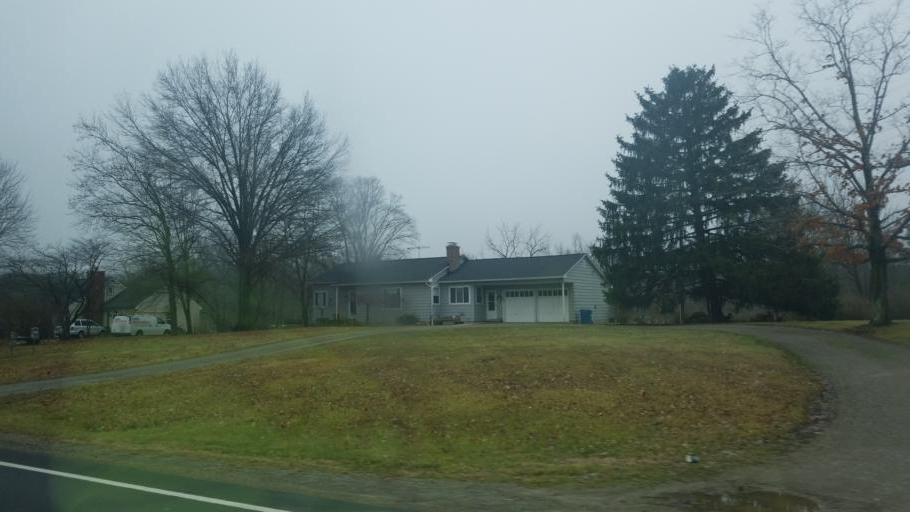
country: US
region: Ohio
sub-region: Union County
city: Marysville
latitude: 40.2476
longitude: -83.4134
